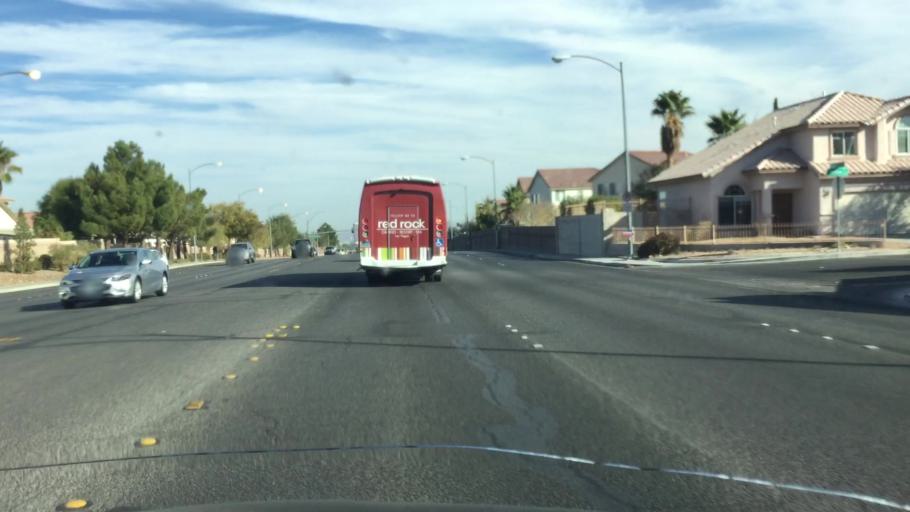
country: US
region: Nevada
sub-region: Clark County
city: Spring Valley
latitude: 36.1292
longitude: -115.2638
